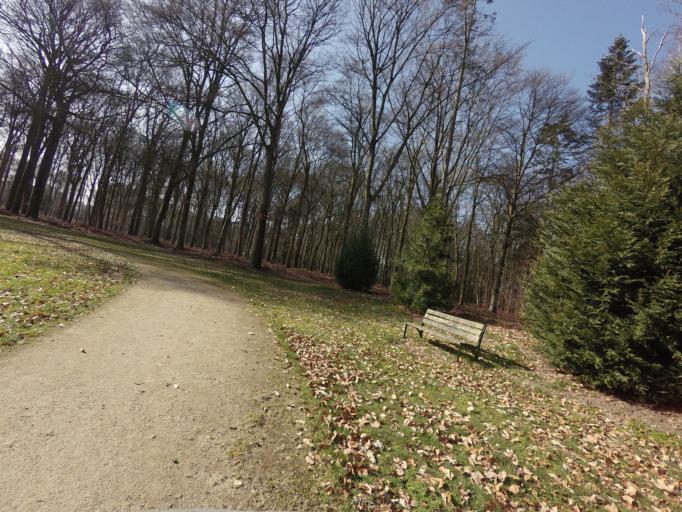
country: NL
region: North Holland
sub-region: Gemeente Wijdemeren
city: Kortenhoef
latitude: 52.2310
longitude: 5.1330
